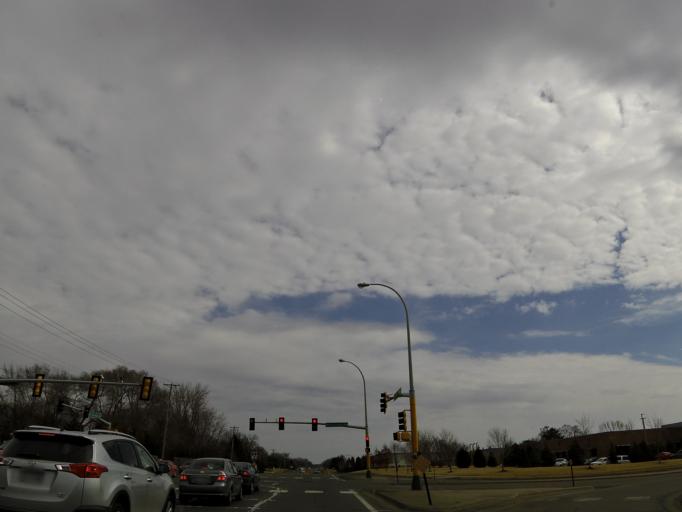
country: US
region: Minnesota
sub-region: Scott County
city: Savage
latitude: 44.8079
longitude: -93.3773
